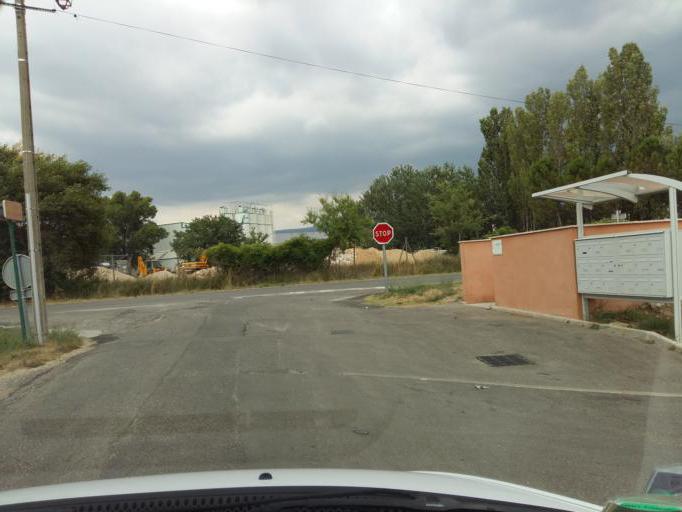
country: FR
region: Provence-Alpes-Cote d'Azur
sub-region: Departement du Vaucluse
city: Gargas
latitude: 43.8910
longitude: 5.3704
